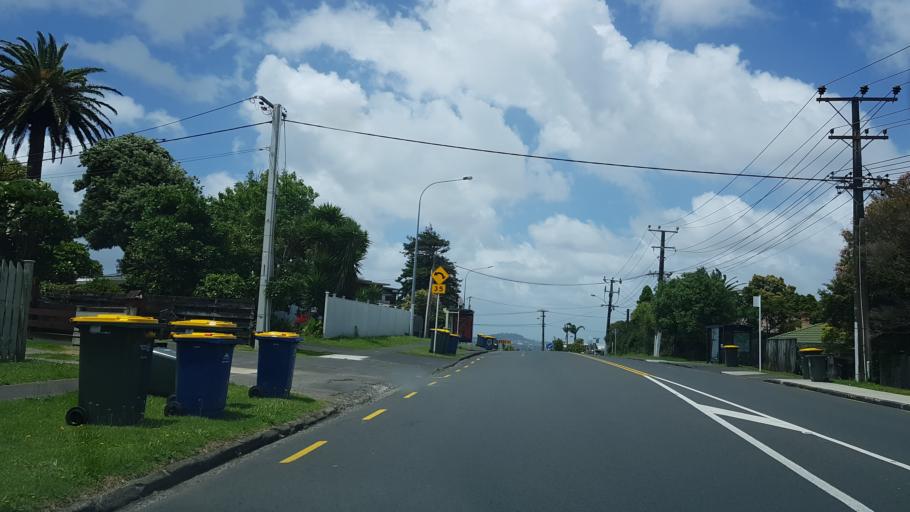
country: NZ
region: Auckland
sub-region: Auckland
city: North Shore
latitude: -36.8099
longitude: 174.7094
